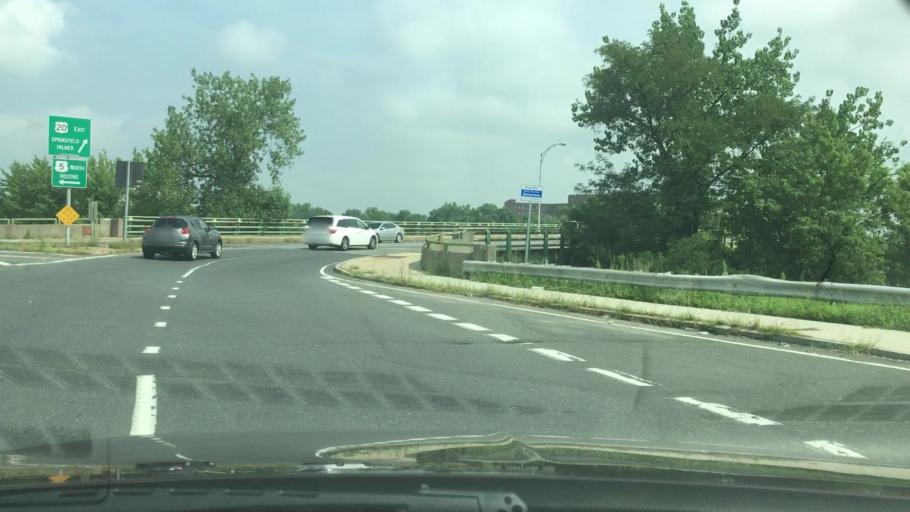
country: US
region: Massachusetts
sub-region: Hampden County
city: West Springfield
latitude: 42.1074
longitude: -72.6158
